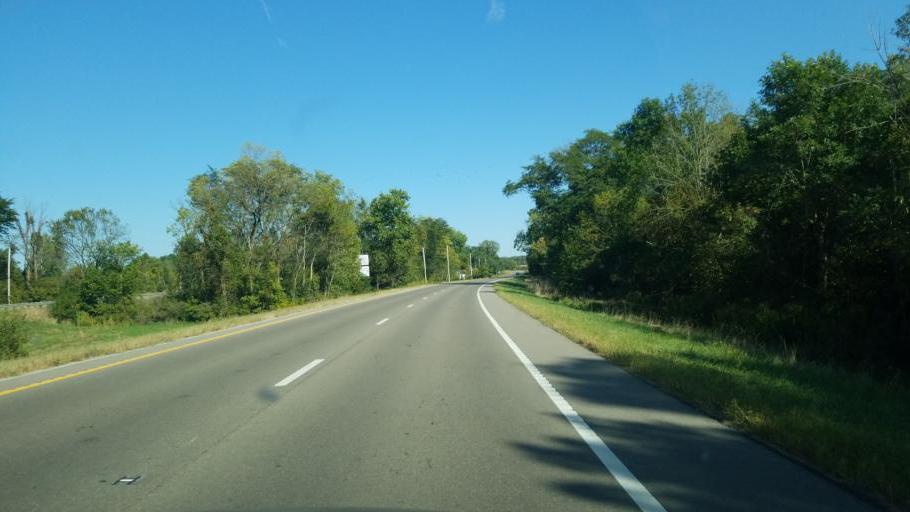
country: US
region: Ohio
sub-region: Clark County
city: Lisbon
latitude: 39.9252
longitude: -83.6705
